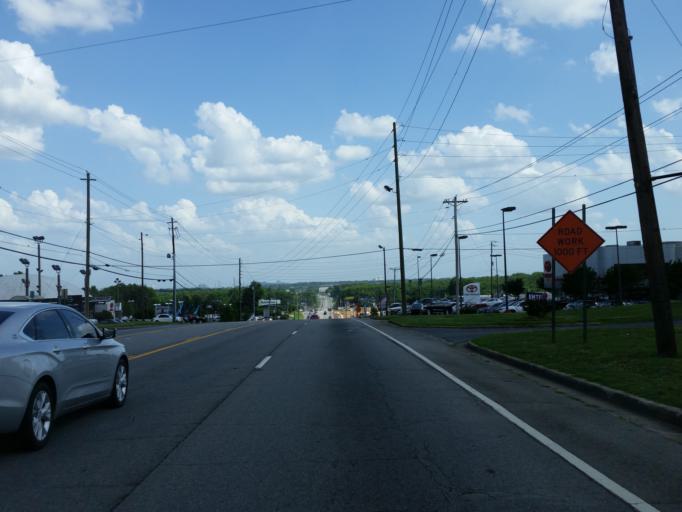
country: US
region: Georgia
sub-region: Cobb County
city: Fair Oaks
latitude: 33.9361
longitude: -84.5127
